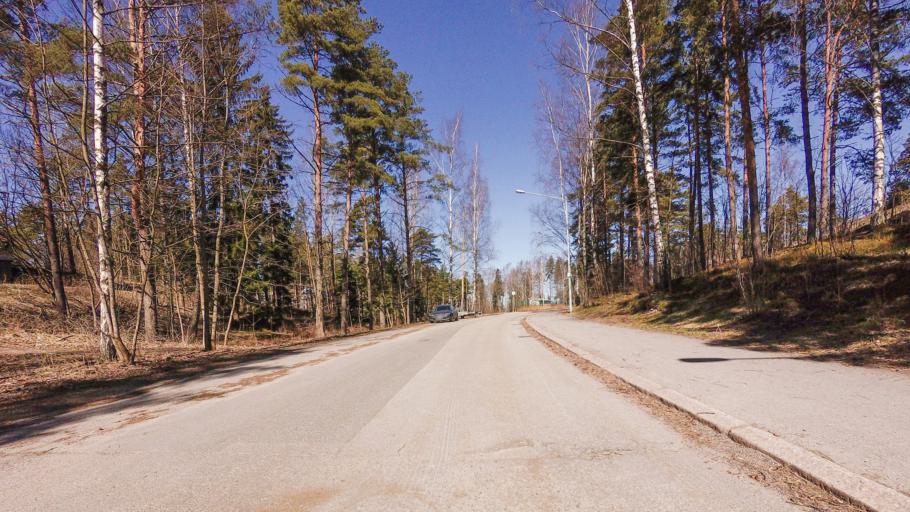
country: FI
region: Uusimaa
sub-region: Helsinki
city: Helsinki
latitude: 60.1765
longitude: 25.0424
